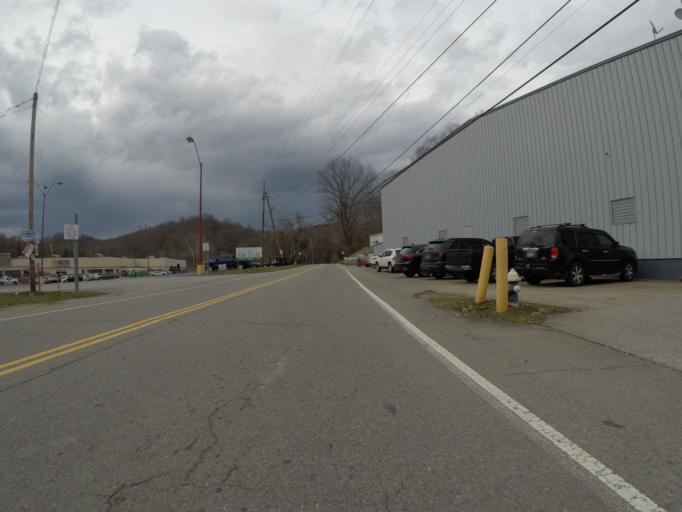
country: US
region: Ohio
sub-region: Lawrence County
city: Burlington
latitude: 38.4202
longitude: -82.5038
